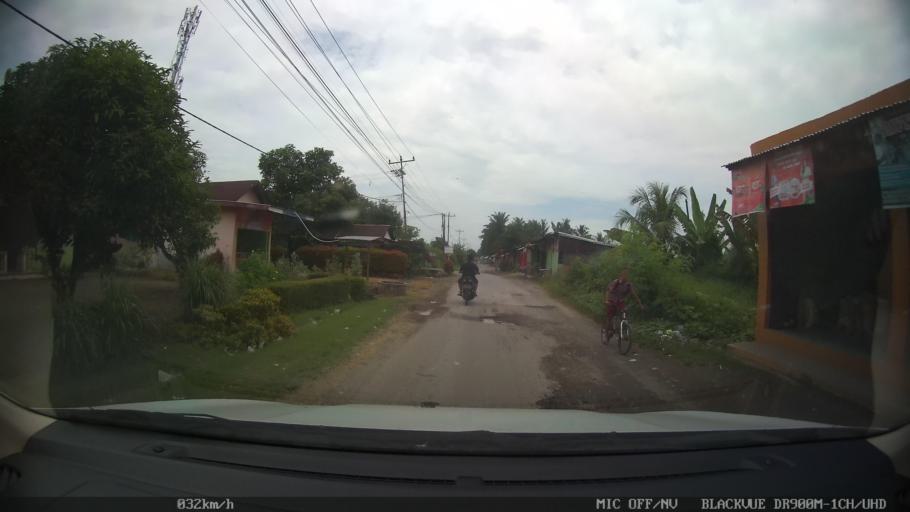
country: ID
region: North Sumatra
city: Sunggal
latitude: 3.6317
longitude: 98.5638
